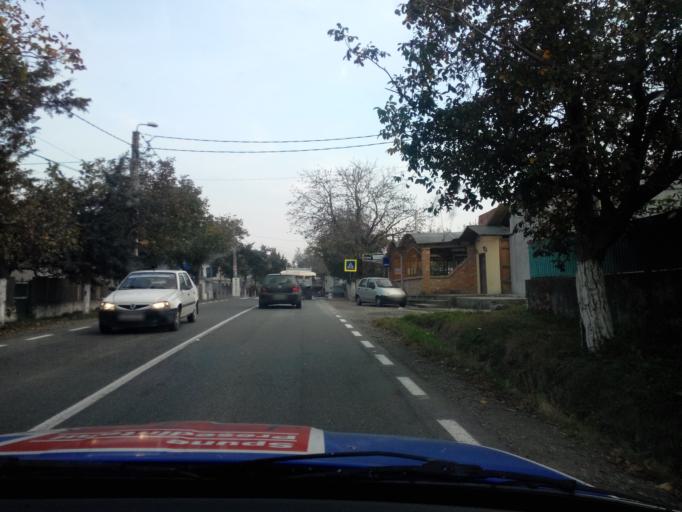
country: RO
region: Tulcea
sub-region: Comuna Somova
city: Somova
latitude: 45.1876
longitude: 28.6635
